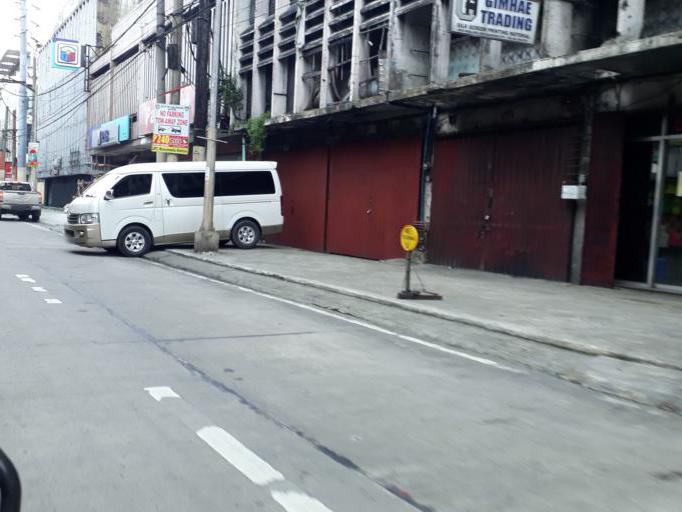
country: PH
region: Calabarzon
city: Del Monte
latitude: 14.6412
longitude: 120.9836
